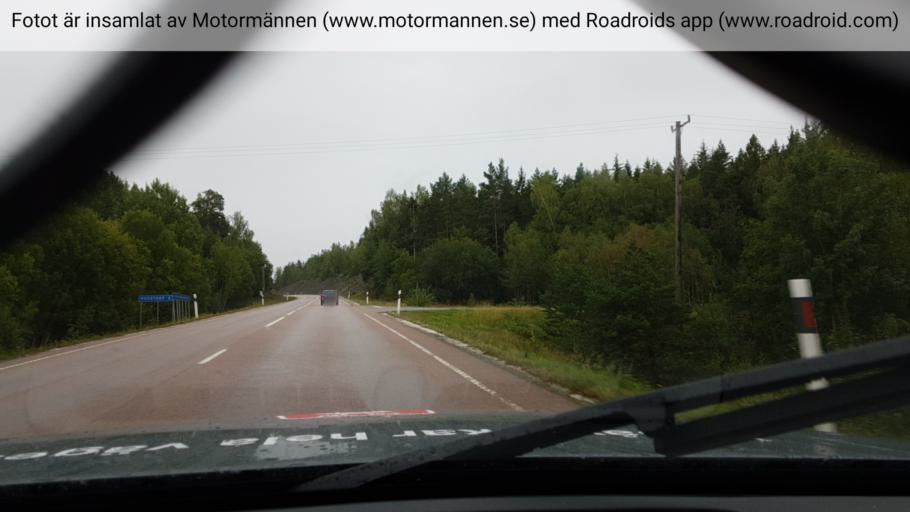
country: SE
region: Soedermanland
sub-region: Eskilstuna Kommun
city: Arla
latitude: 59.2424
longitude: 16.6019
